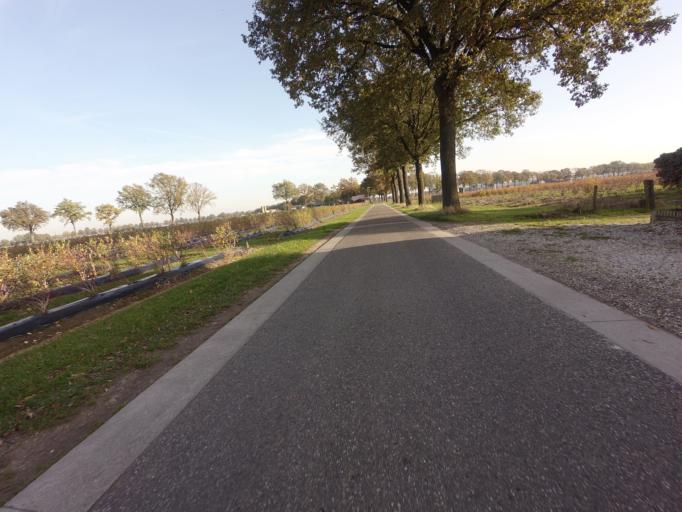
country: NL
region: Limburg
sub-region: Gemeente Roerdalen
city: Montfort
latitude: 51.1117
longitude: 5.9559
